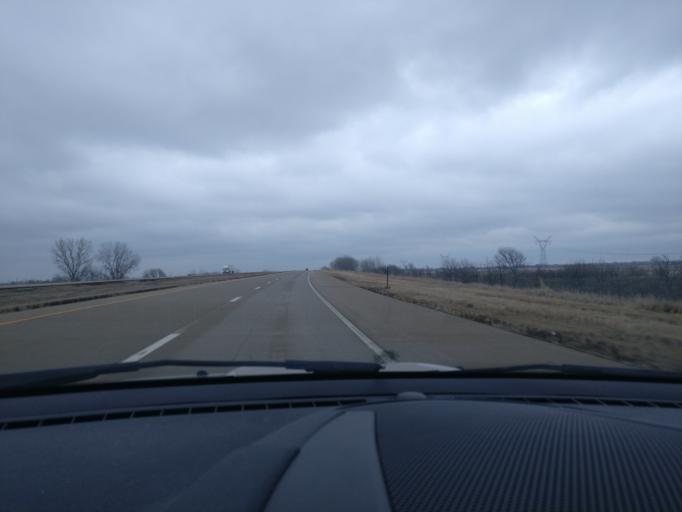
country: US
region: Illinois
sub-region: Whiteside County
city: Morrison
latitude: 41.7653
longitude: -89.8390
